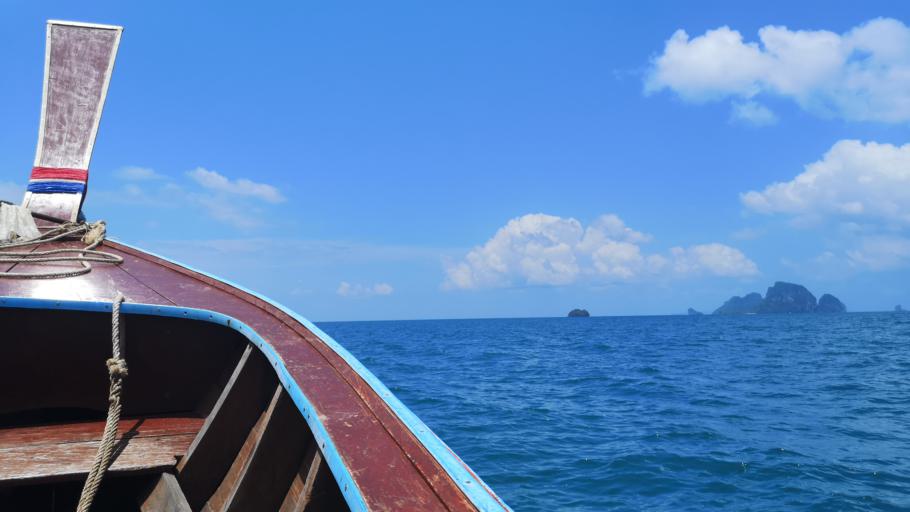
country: TH
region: Phangnga
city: Ban Ao Nang
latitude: 8.0224
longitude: 98.8217
